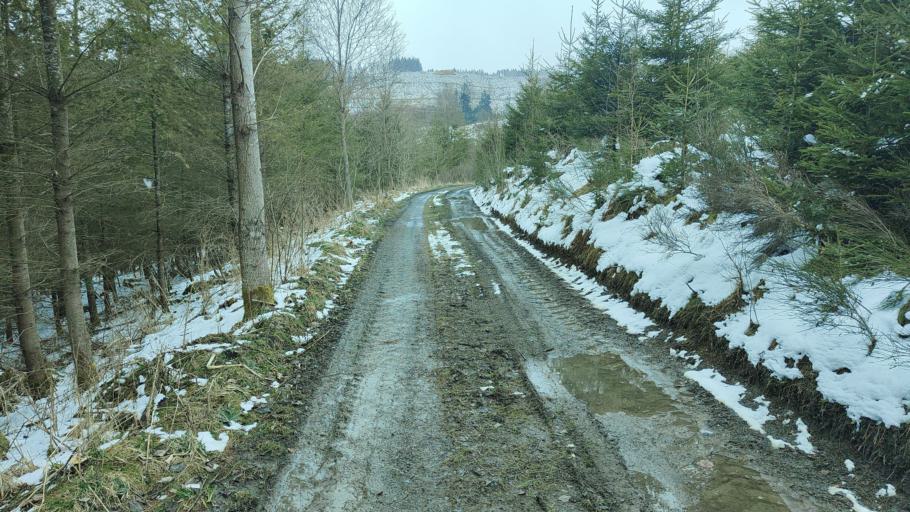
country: DE
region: North Rhine-Westphalia
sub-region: Regierungsbezirk Arnsberg
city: Bad Berleburg
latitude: 51.0845
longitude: 8.4278
